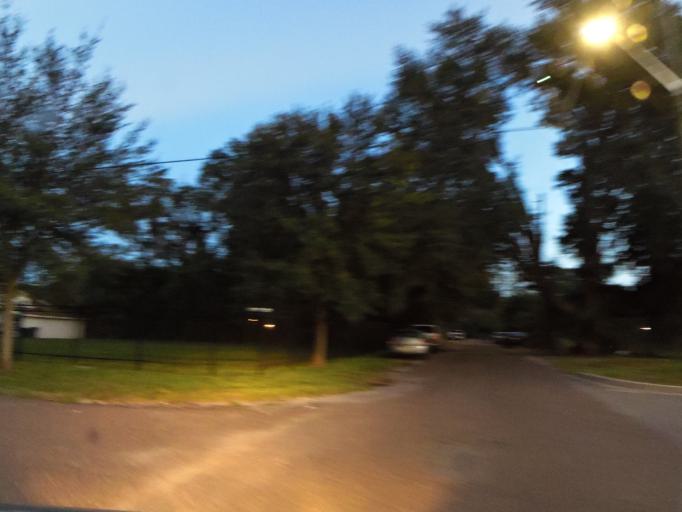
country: US
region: Florida
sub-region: Duval County
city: Jacksonville
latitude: 30.3569
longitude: -81.6355
